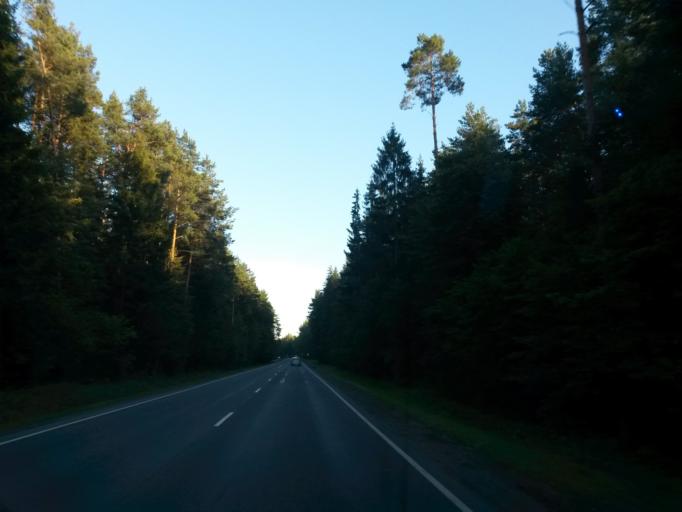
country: RU
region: Moskovskaya
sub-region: Podol'skiy Rayon
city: Podol'sk
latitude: 55.3806
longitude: 37.6332
